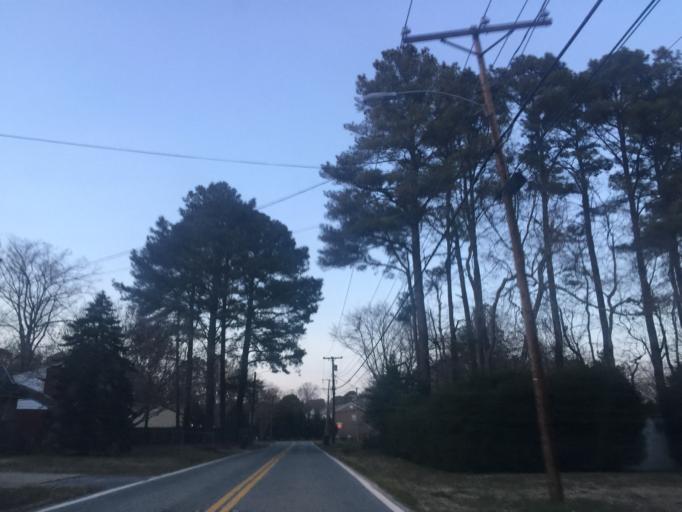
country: US
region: Virginia
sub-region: City of Newport News
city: Newport News
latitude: 37.0752
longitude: -76.5084
